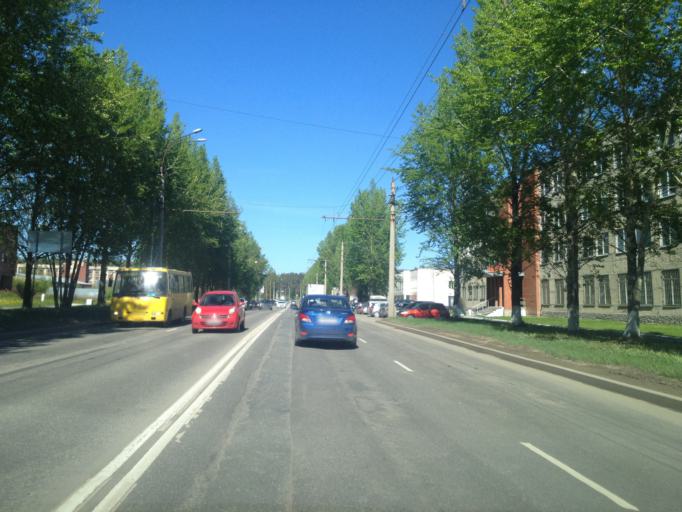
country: RU
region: Sverdlovsk
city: Sovkhoznyy
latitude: 56.7773
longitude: 60.5539
